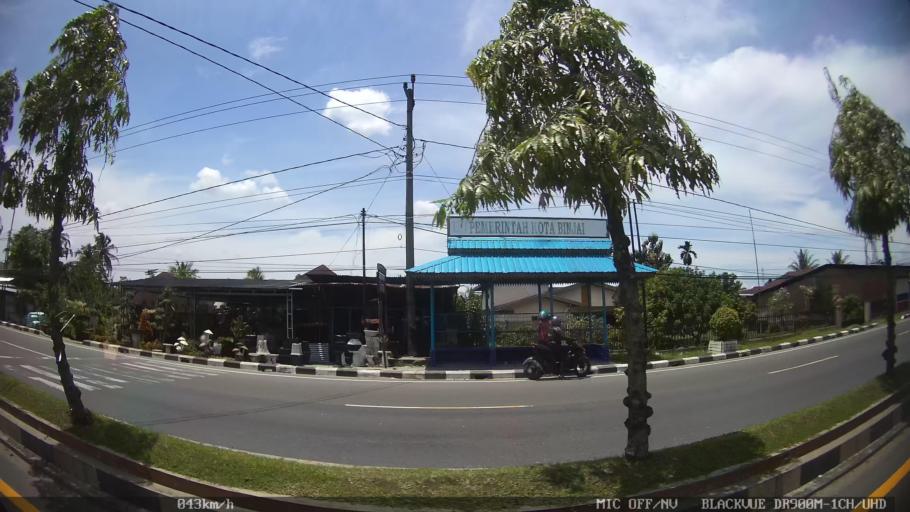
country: ID
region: North Sumatra
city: Binjai
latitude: 3.6086
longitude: 98.5142
